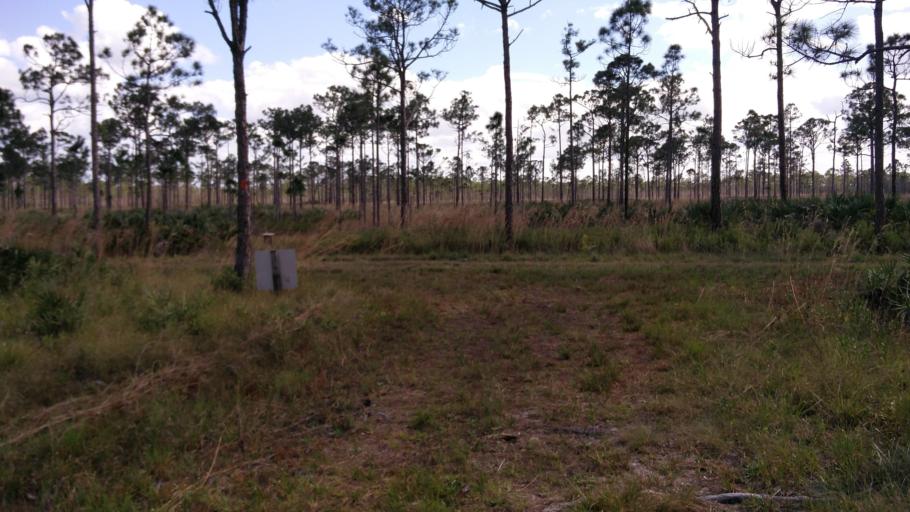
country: US
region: Florida
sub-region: Martin County
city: Hobe Sound
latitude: 27.0198
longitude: -80.1493
